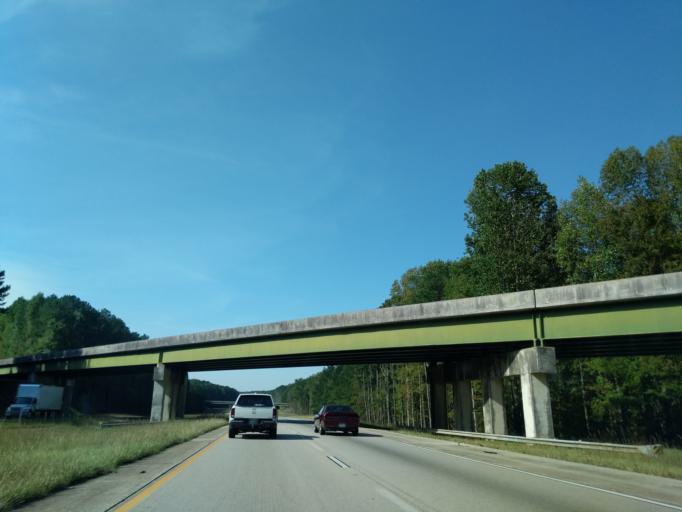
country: US
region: Georgia
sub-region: Troup County
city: La Grange
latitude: 33.0617
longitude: -84.9446
